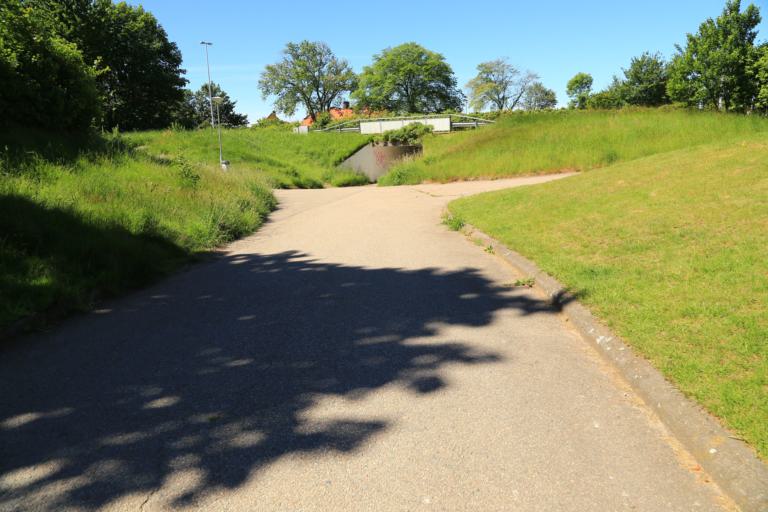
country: SE
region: Halland
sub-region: Varbergs Kommun
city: Varberg
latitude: 57.1150
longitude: 12.2615
